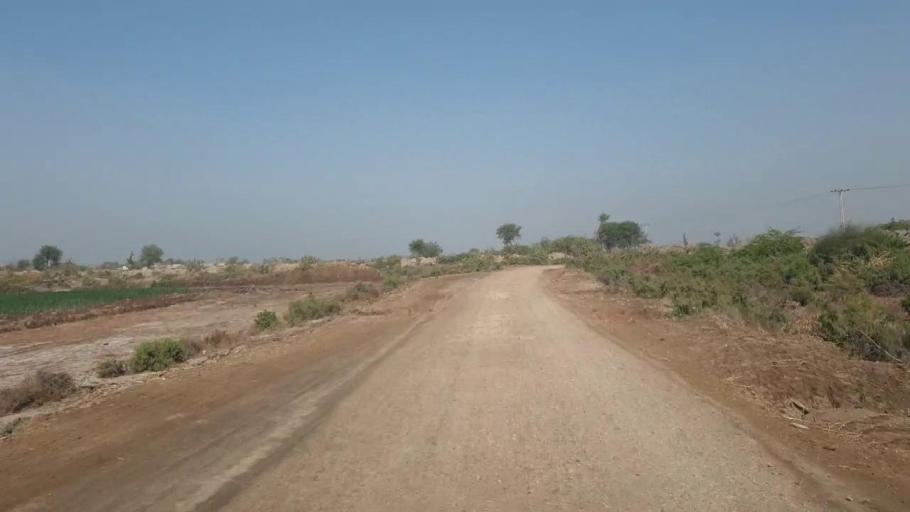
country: PK
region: Sindh
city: Mirwah Gorchani
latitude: 25.3732
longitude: 69.1869
